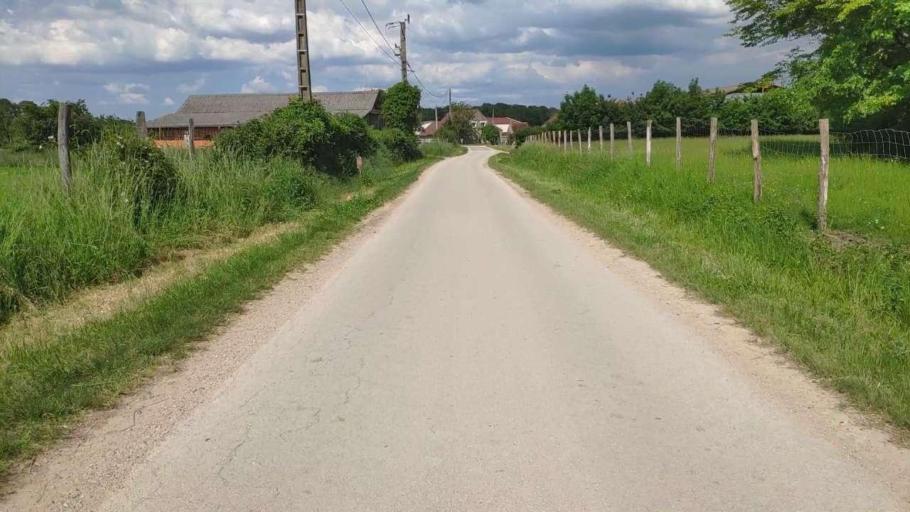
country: FR
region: Franche-Comte
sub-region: Departement du Jura
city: Bletterans
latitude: 46.8256
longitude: 5.4060
